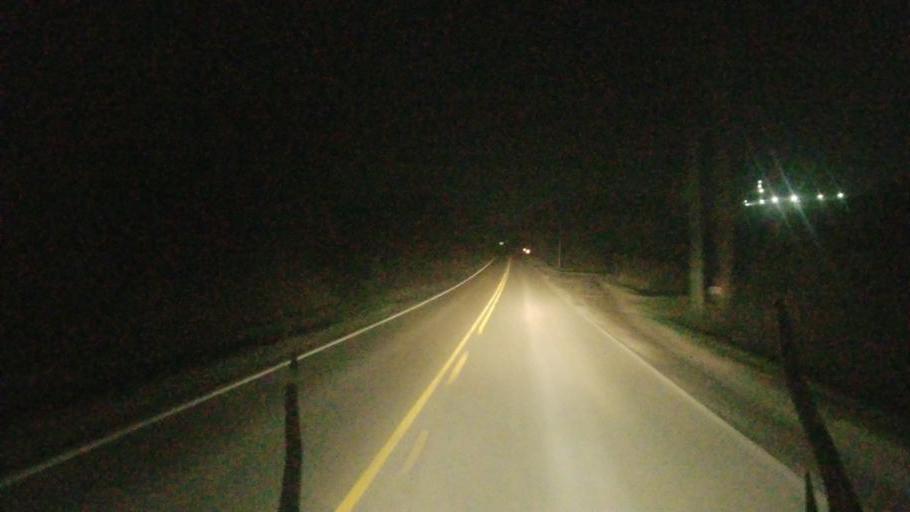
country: US
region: Ohio
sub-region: Harrison County
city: Cadiz
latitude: 40.2565
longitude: -81.0345
